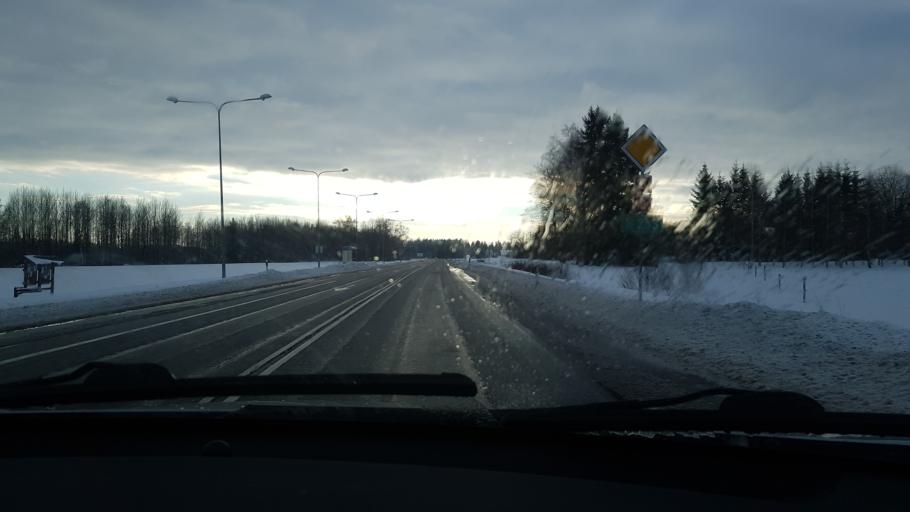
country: EE
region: Jaervamaa
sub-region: Paide linn
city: Paide
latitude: 58.9395
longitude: 25.6396
